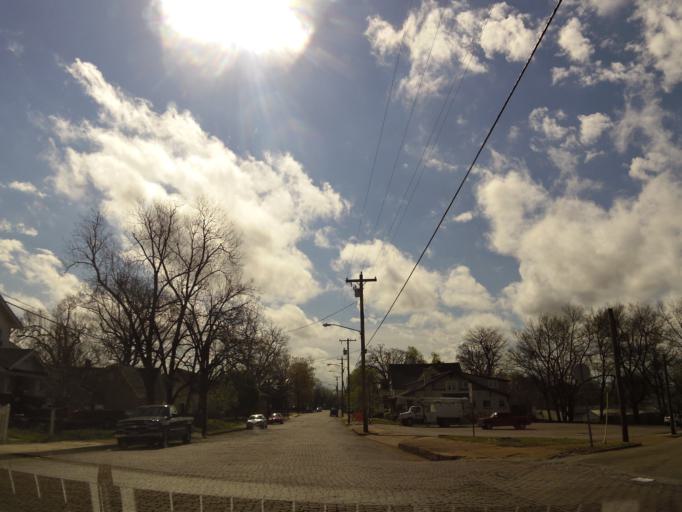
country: US
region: Missouri
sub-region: Butler County
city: Poplar Bluff
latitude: 36.7616
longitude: -90.3956
